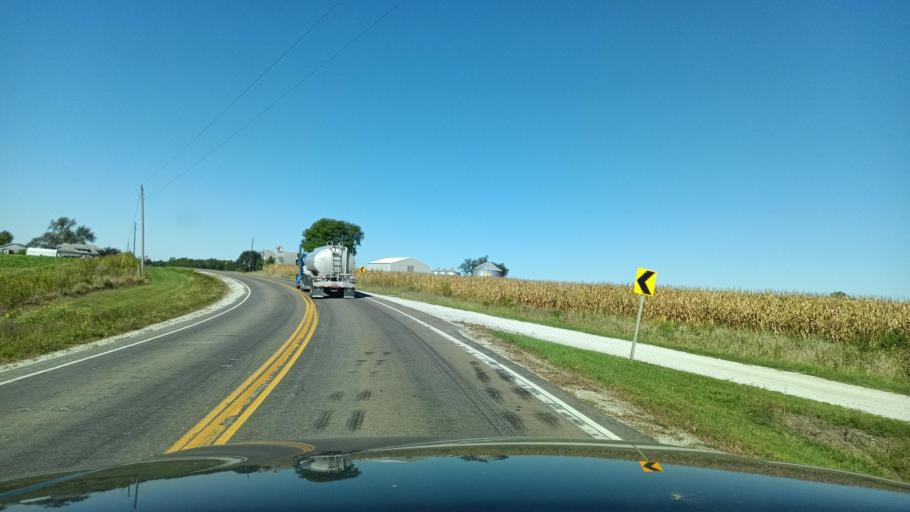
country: US
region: Missouri
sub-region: Scotland County
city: Memphis
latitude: 40.4556
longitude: -92.1102
